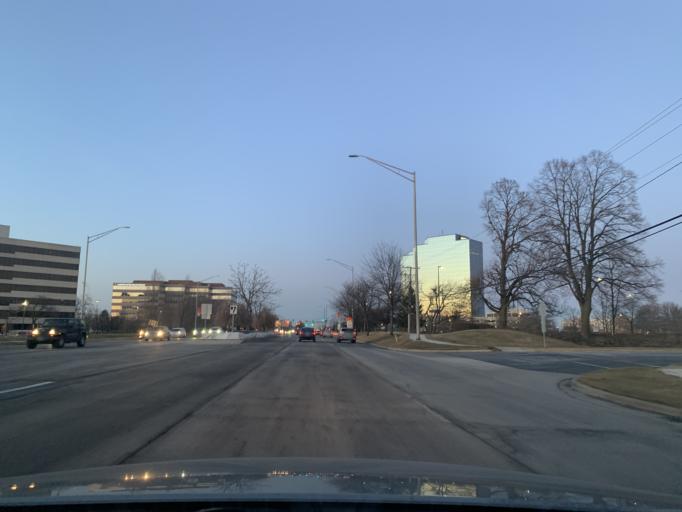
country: US
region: Illinois
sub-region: Cook County
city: Hoffman Estates
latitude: 42.0409
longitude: -88.0453
